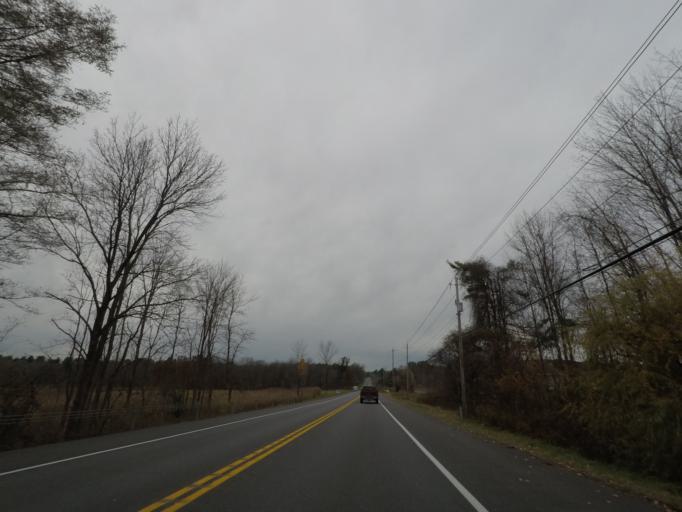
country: US
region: New York
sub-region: Saratoga County
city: Mechanicville
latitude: 42.8652
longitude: -73.7403
